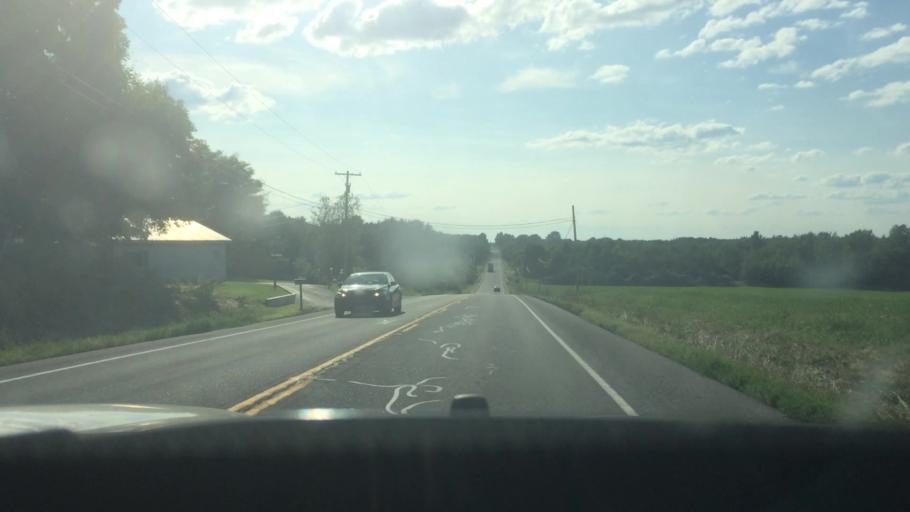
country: US
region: New York
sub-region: St. Lawrence County
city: Potsdam
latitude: 44.6894
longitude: -74.7295
